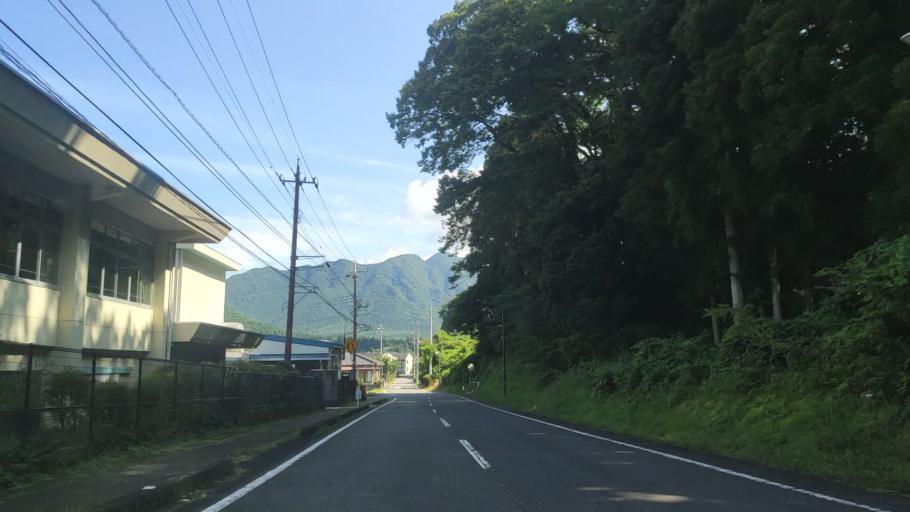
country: JP
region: Tochigi
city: Imaichi
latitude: 36.8416
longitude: 139.7254
